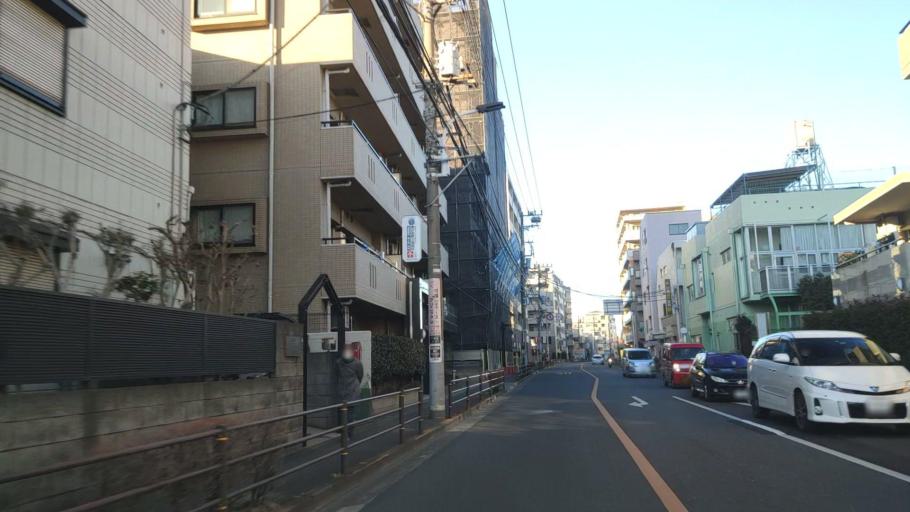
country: JP
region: Tokyo
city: Mitaka-shi
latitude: 35.6922
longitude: 139.5646
